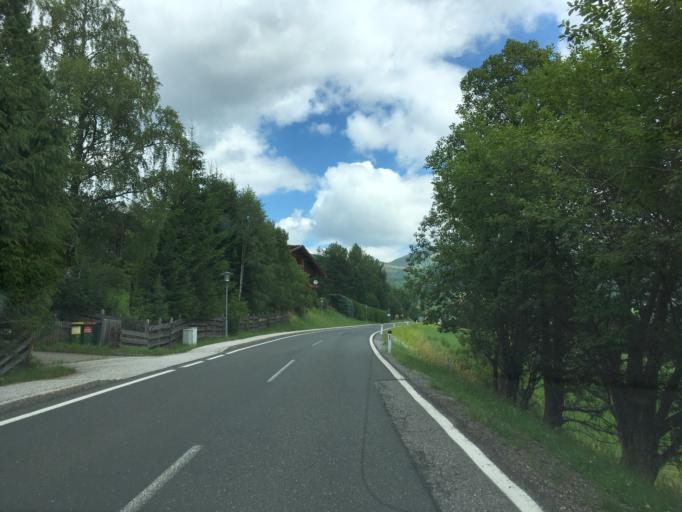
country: AT
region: Carinthia
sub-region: Politischer Bezirk Spittal an der Drau
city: Kleinkirchheim
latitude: 46.8324
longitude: 13.7636
